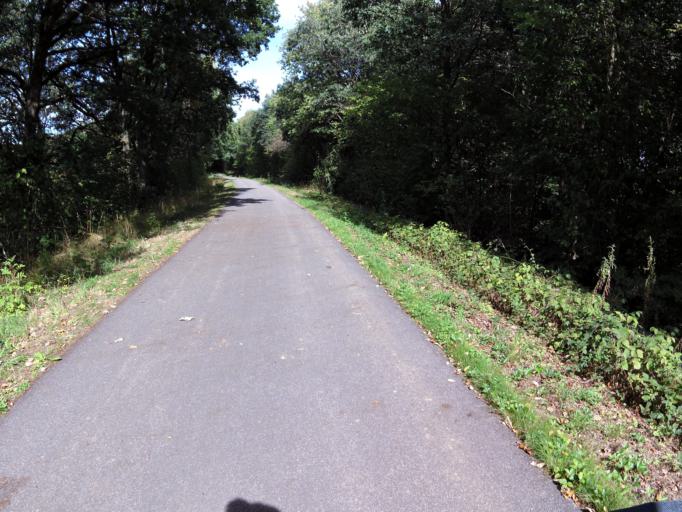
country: DE
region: Rheinland-Pfalz
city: Arzfeld
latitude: 50.1024
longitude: 6.2715
